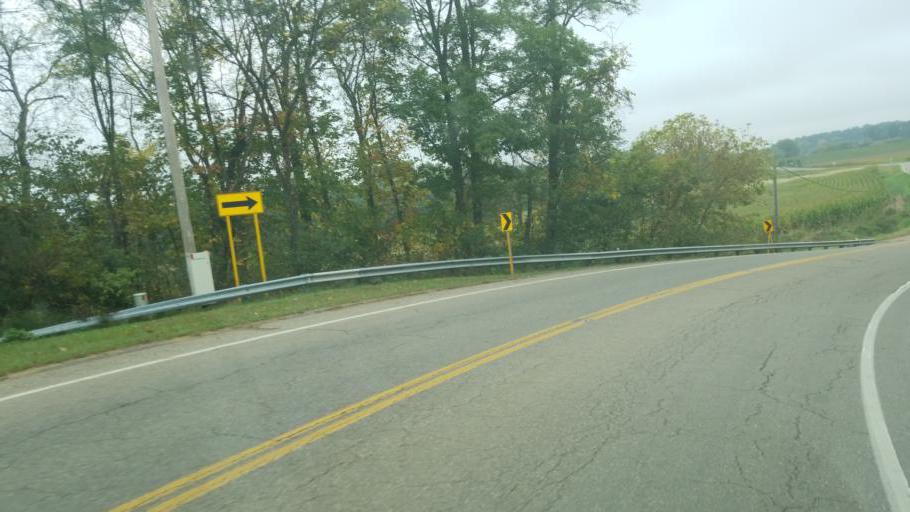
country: US
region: Ohio
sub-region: Carroll County
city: Lake Mohawk
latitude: 40.6433
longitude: -81.2983
